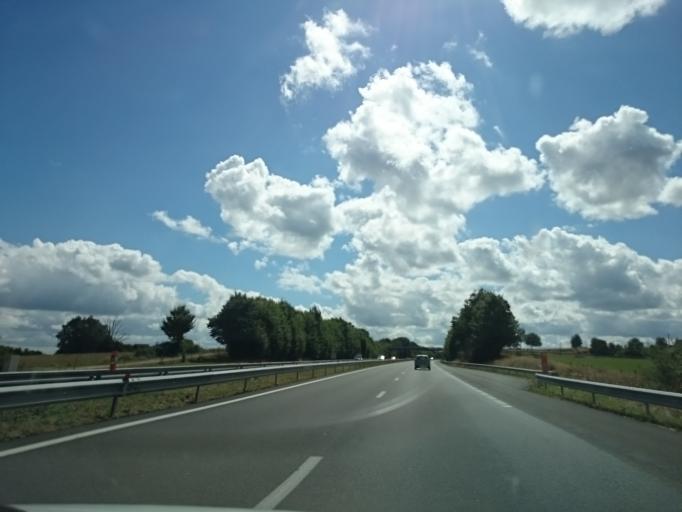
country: FR
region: Pays de la Loire
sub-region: Departement de Maine-et-Loire
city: Durtal
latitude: 47.6833
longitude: -0.2525
